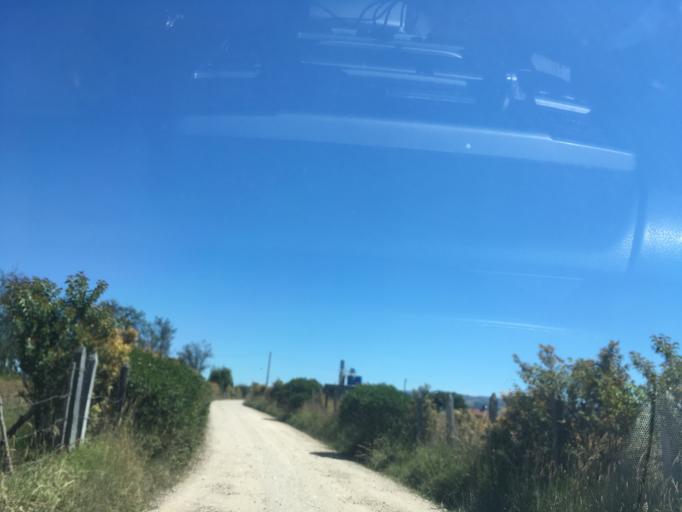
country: CO
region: Boyaca
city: Tuta
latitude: 5.6690
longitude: -73.2738
